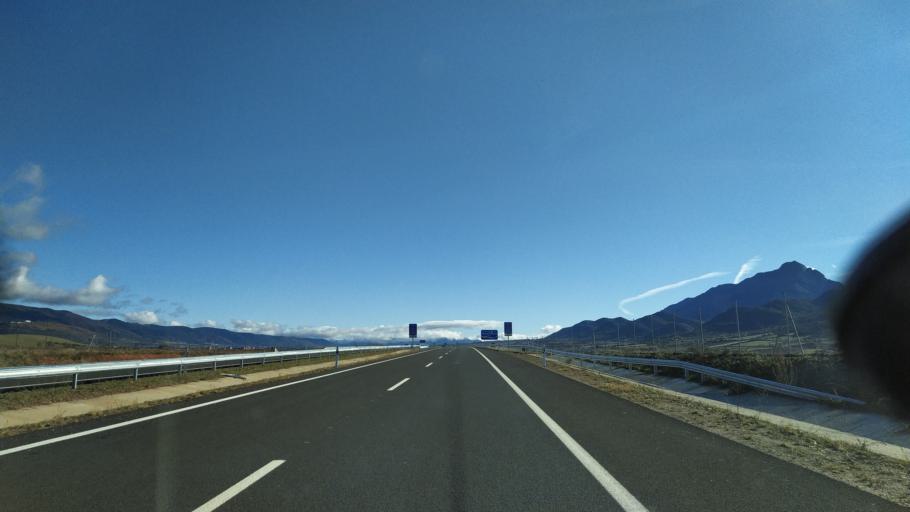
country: ES
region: Aragon
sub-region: Provincia de Huesca
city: Santa Cruz de la Seros
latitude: 42.5635
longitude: -0.6212
